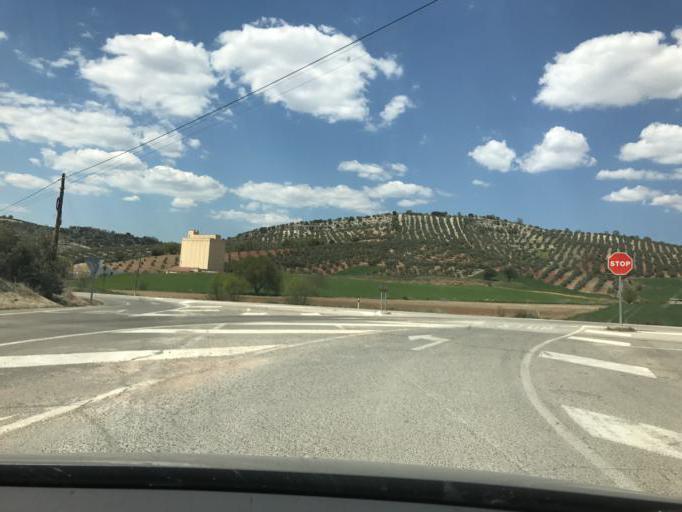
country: ES
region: Andalusia
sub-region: Provincia de Granada
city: Campotejar
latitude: 37.4535
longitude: -3.6271
